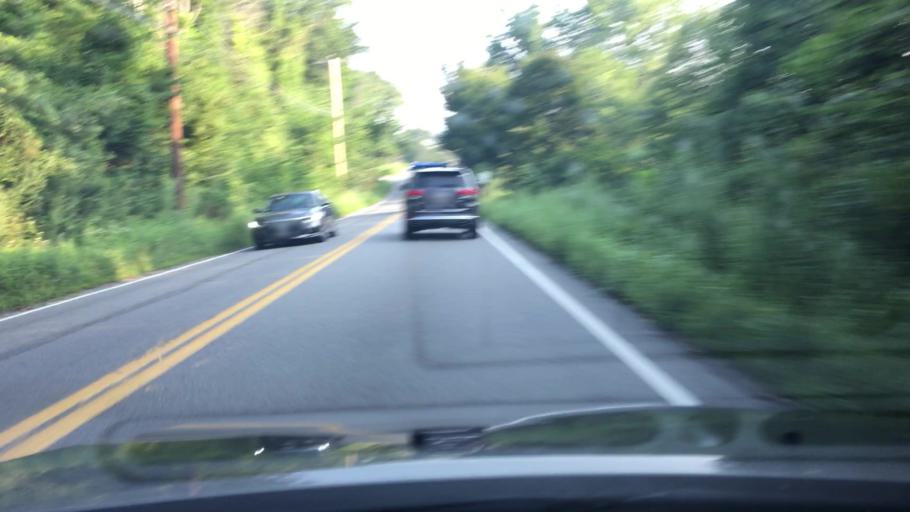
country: US
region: Massachusetts
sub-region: Worcester County
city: Westborough
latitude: 42.2529
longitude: -71.5914
